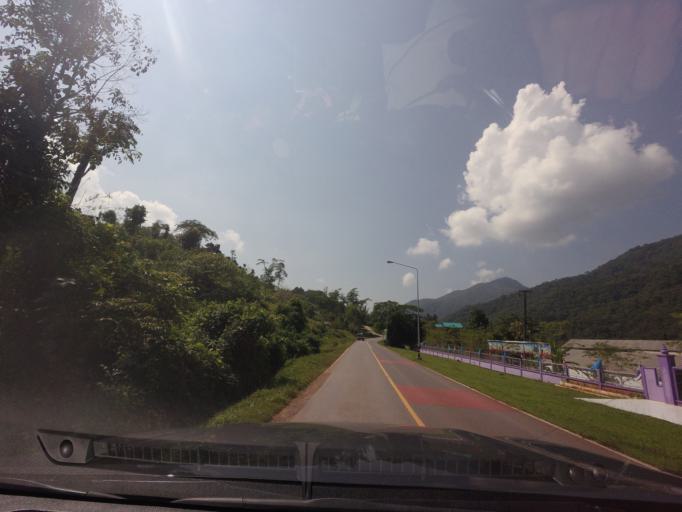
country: TH
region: Nan
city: Bo Kluea
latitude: 19.1429
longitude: 101.1532
